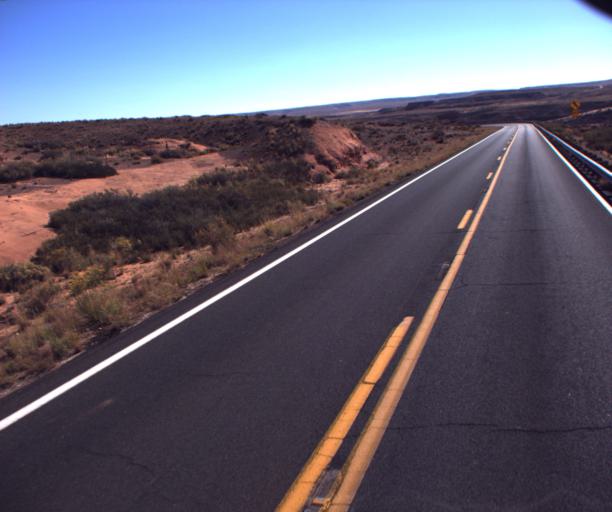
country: US
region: Arizona
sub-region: Coconino County
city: Tuba City
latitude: 36.1066
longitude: -111.2111
